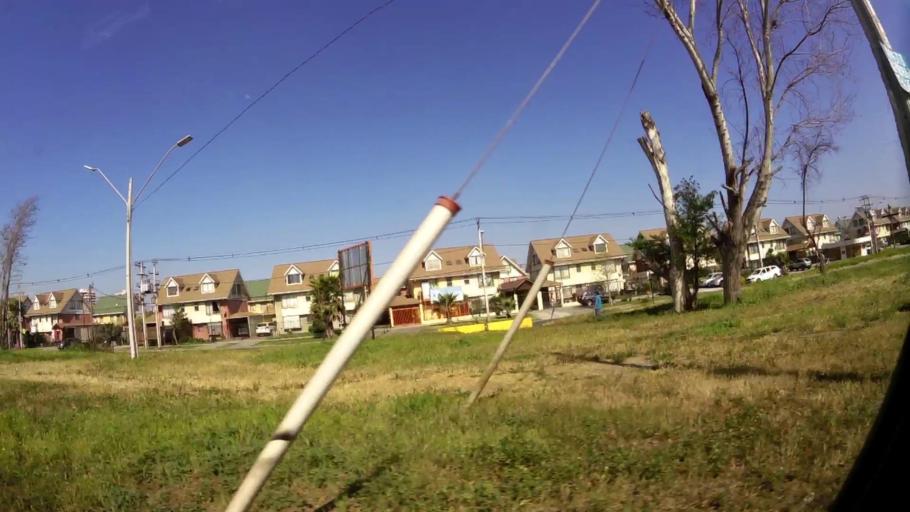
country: CL
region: Santiago Metropolitan
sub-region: Provincia de Santiago
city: Lo Prado
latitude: -33.4804
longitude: -70.7602
